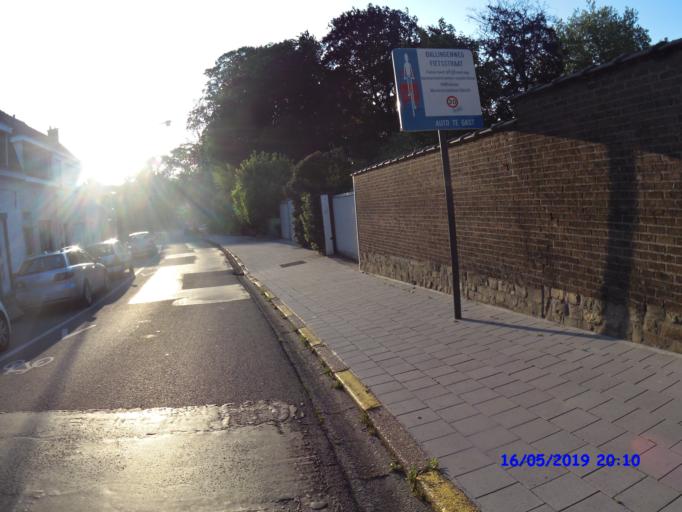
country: BE
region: Flanders
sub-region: Provincie West-Vlaanderen
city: Harelbeke
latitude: 50.8553
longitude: 3.3128
